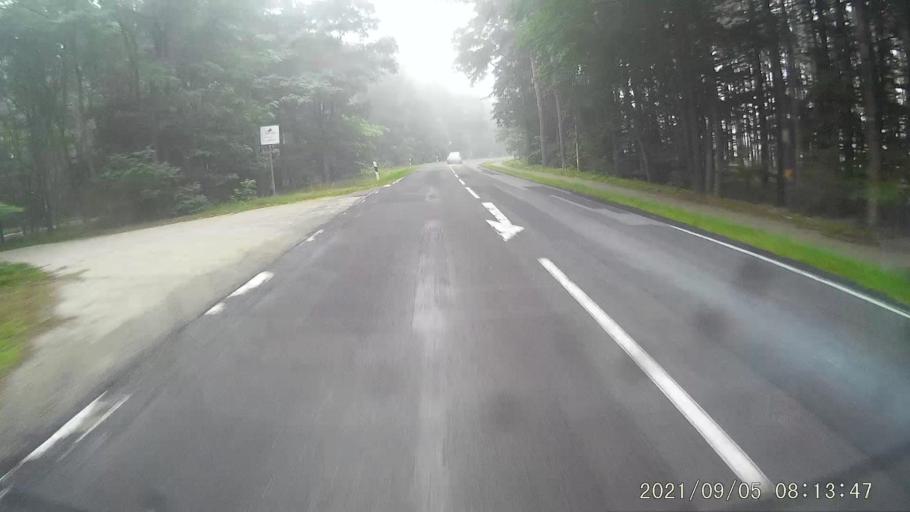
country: DE
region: Saxony
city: Boxberg
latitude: 51.4367
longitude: 14.6025
